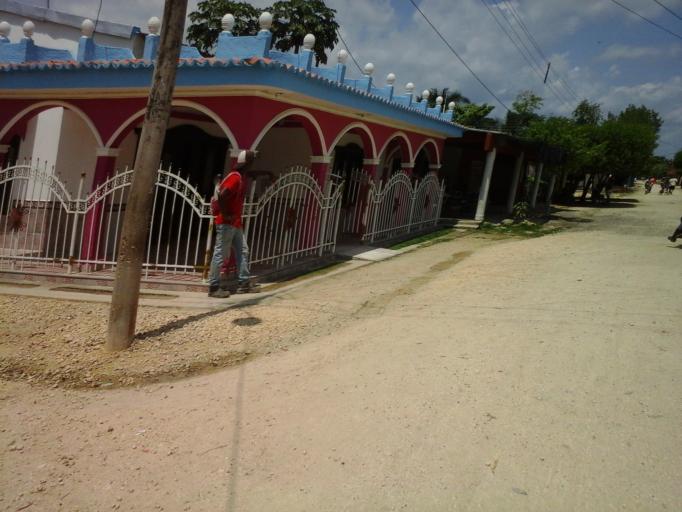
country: CO
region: Bolivar
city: San Pablo
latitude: 10.1432
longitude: -75.2758
